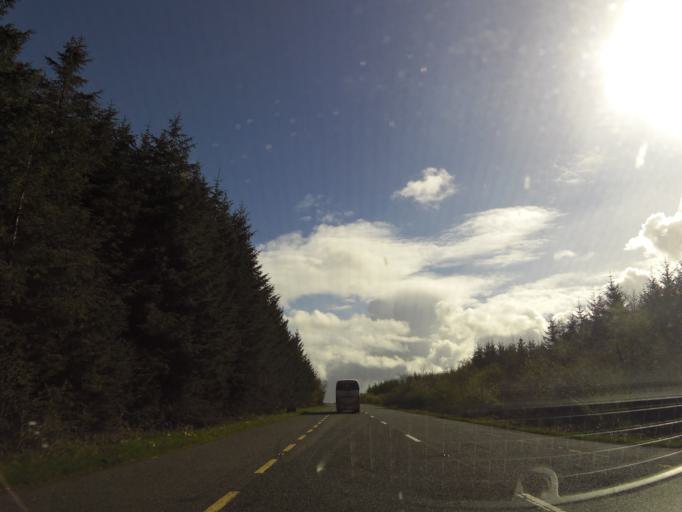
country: IE
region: Connaught
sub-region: Maigh Eo
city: Ballyhaunis
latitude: 53.8822
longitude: -8.8125
